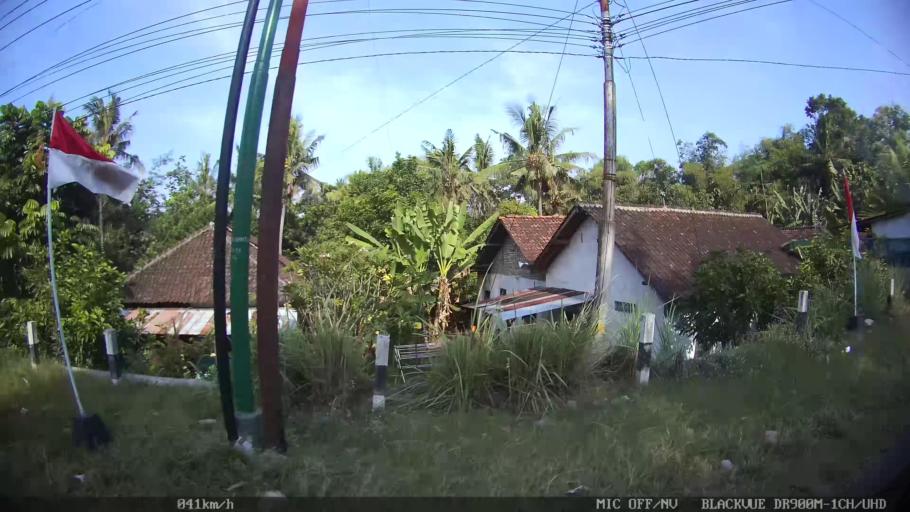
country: ID
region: Daerah Istimewa Yogyakarta
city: Bantul
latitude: -7.8796
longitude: 110.3141
